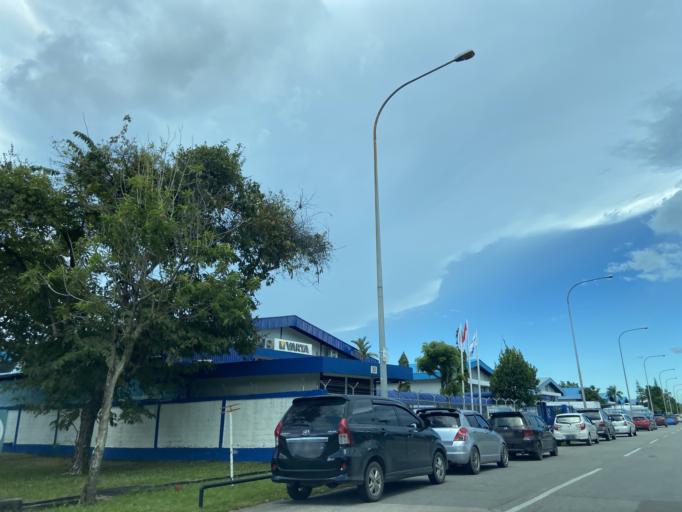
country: SG
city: Singapore
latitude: 1.0640
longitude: 104.0275
